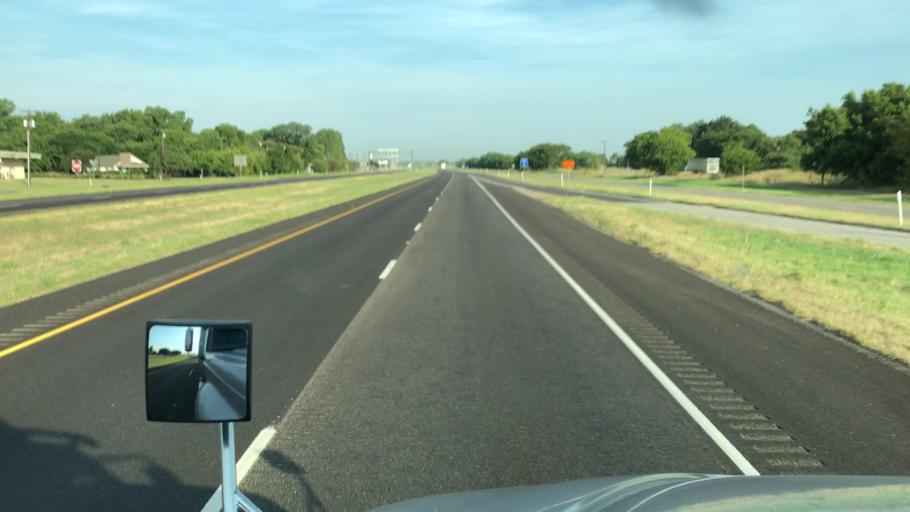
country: US
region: Texas
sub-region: McLennan County
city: Bellmead
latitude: 31.5482
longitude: -97.0726
